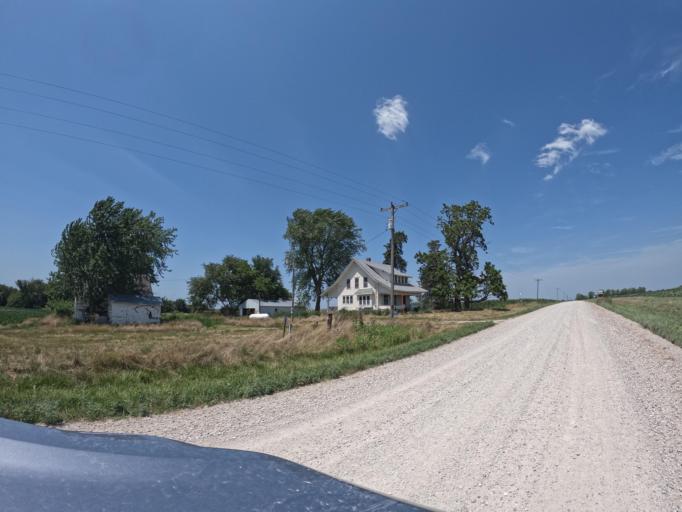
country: US
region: Iowa
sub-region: Henry County
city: Mount Pleasant
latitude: 40.9372
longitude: -91.6457
